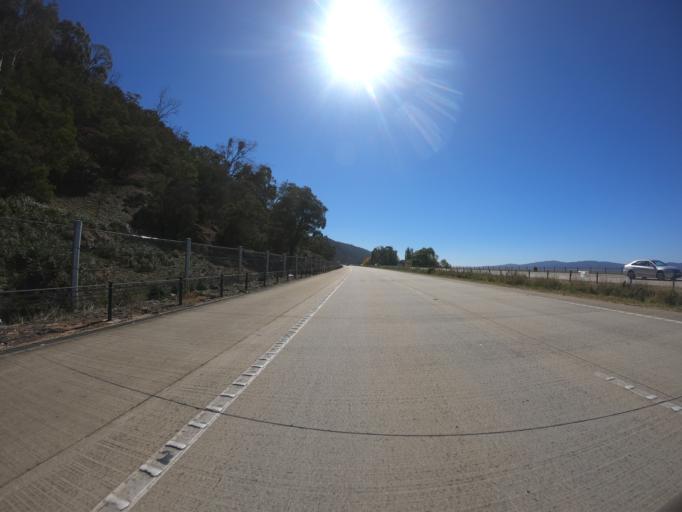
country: AU
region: New South Wales
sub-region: Yass Valley
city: Gundaroo
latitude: -35.0757
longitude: 149.3744
